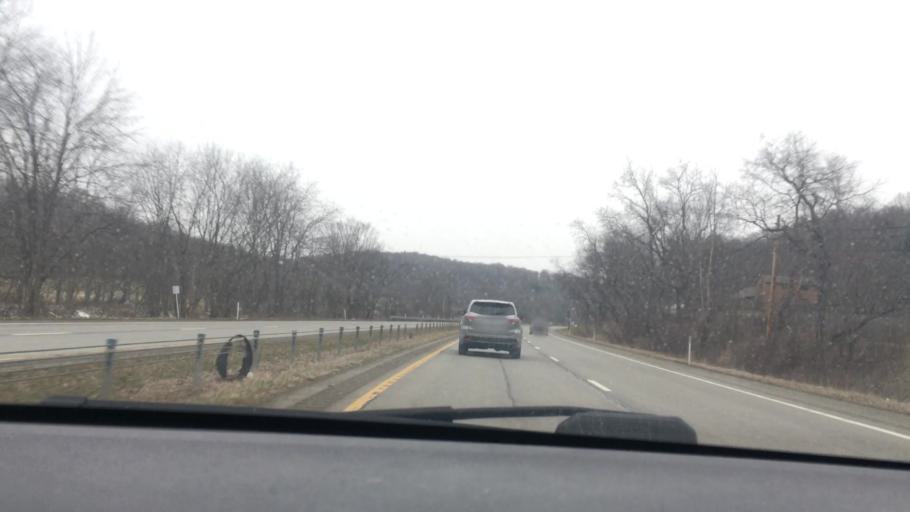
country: US
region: Pennsylvania
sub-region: Beaver County
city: Big Beaver
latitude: 40.8059
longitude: -80.4485
